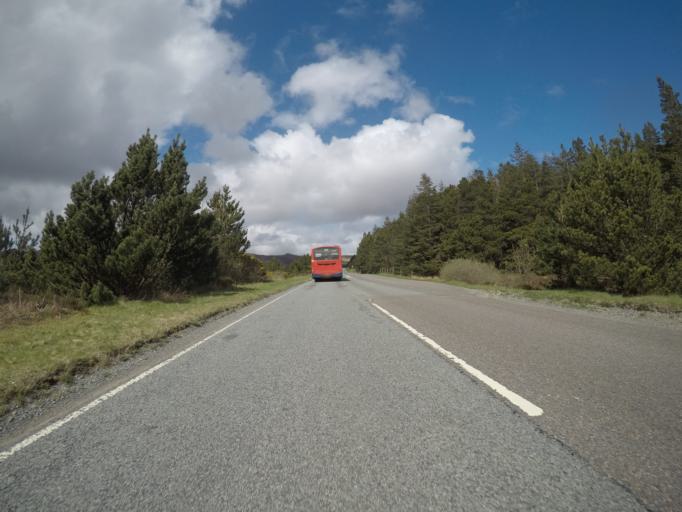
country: GB
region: Scotland
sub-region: Highland
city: Isle of Skye
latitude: 57.3147
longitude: -6.1997
